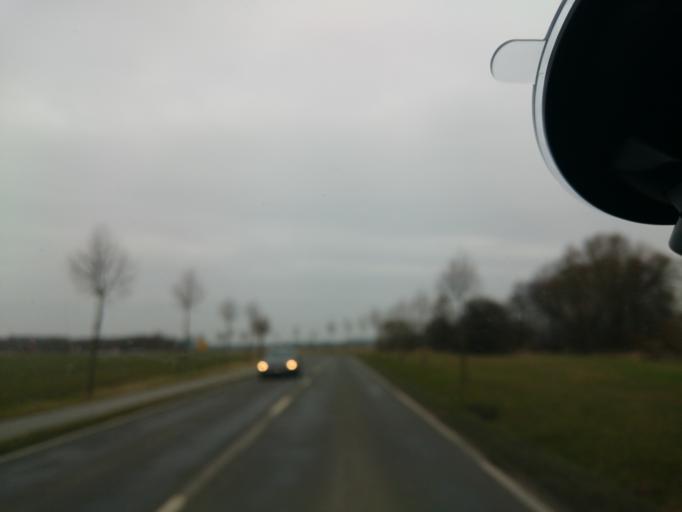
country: DE
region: Mecklenburg-Vorpommern
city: Bad Doberan
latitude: 54.1142
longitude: 11.9175
